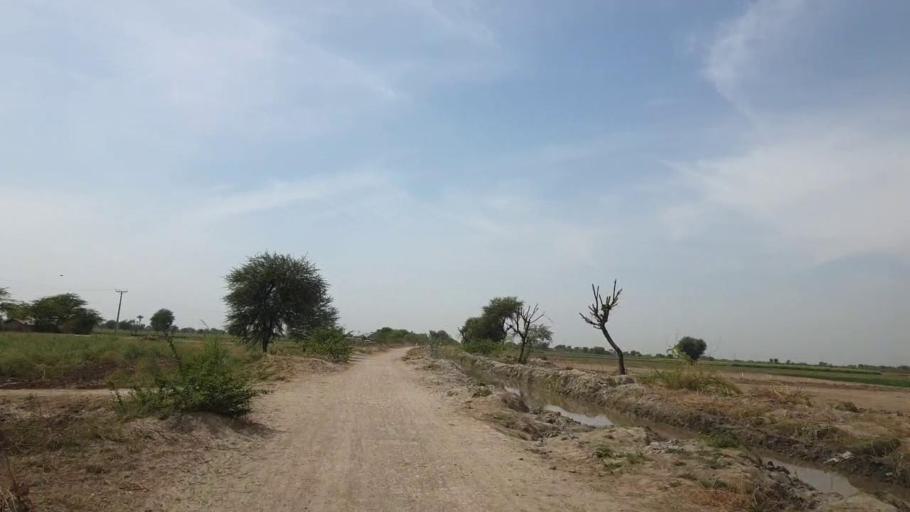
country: PK
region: Sindh
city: Kunri
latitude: 25.1945
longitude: 69.5820
